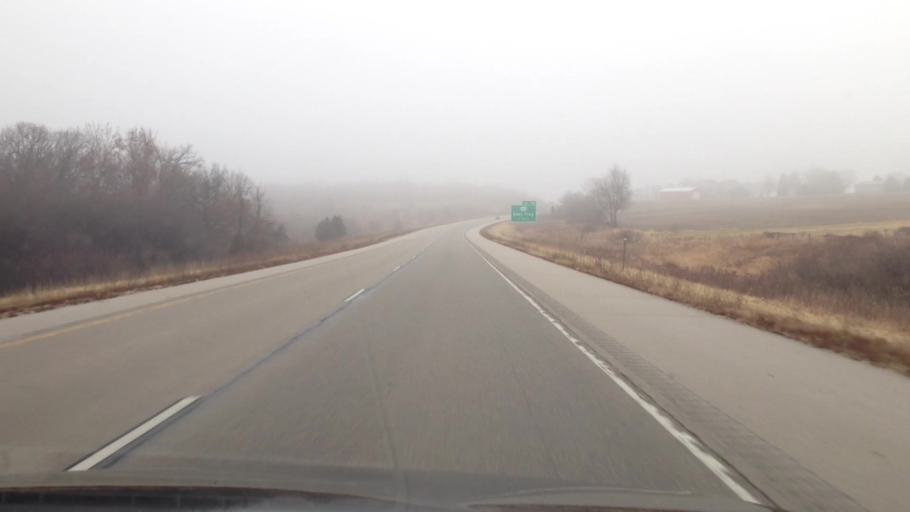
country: US
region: Wisconsin
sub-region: Walworth County
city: East Troy
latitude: 42.7609
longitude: -88.4311
